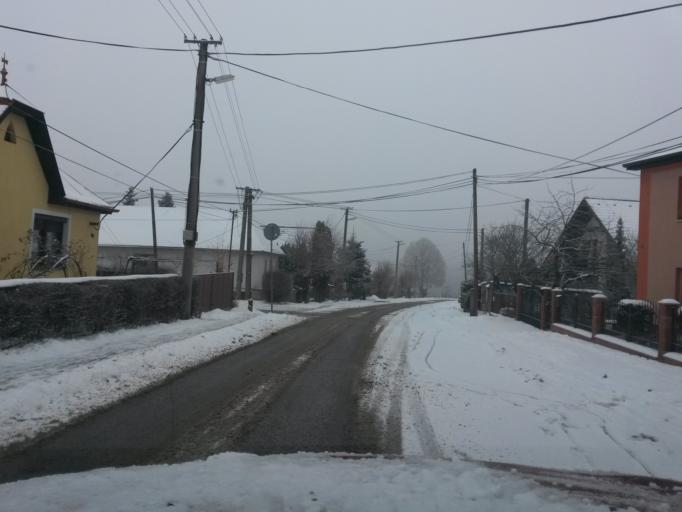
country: SK
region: Kosicky
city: Kosice
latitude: 48.7284
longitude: 21.3038
